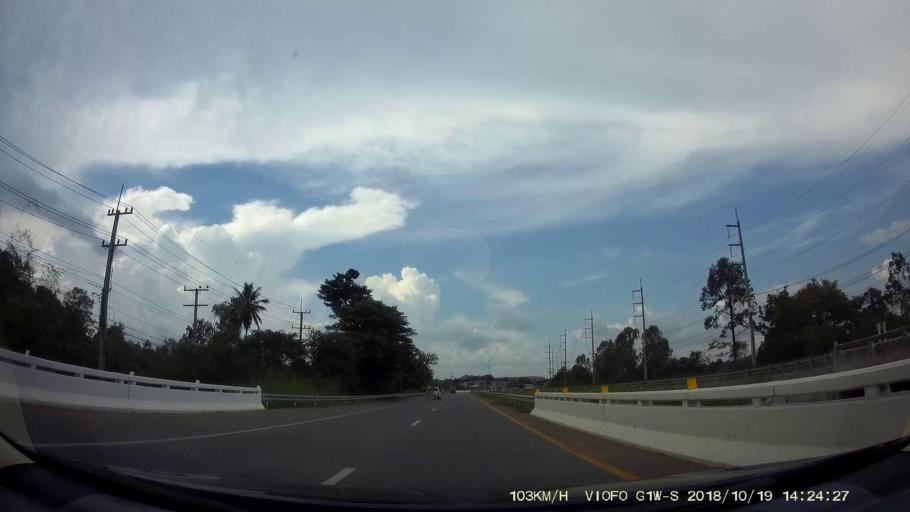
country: TH
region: Chaiyaphum
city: Kaeng Khro
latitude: 16.0808
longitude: 102.2725
